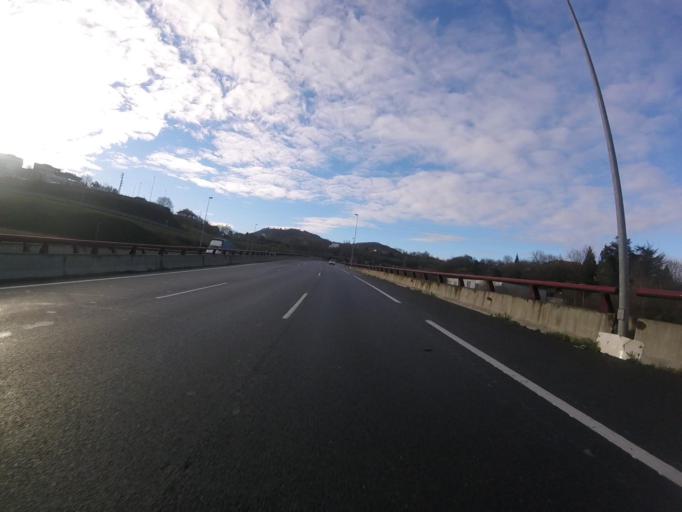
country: ES
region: Basque Country
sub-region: Provincia de Guipuzcoa
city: Errenteria
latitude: 43.3116
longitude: -1.9176
